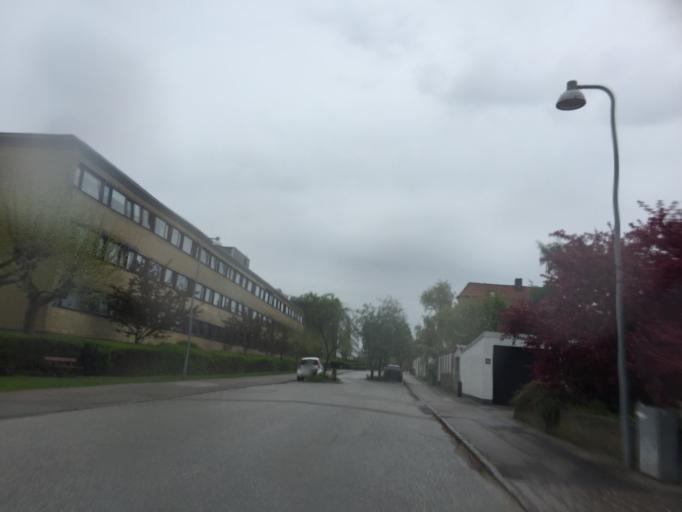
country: DK
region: Capital Region
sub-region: Frederiksberg Kommune
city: Frederiksberg
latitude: 55.6920
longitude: 12.5223
